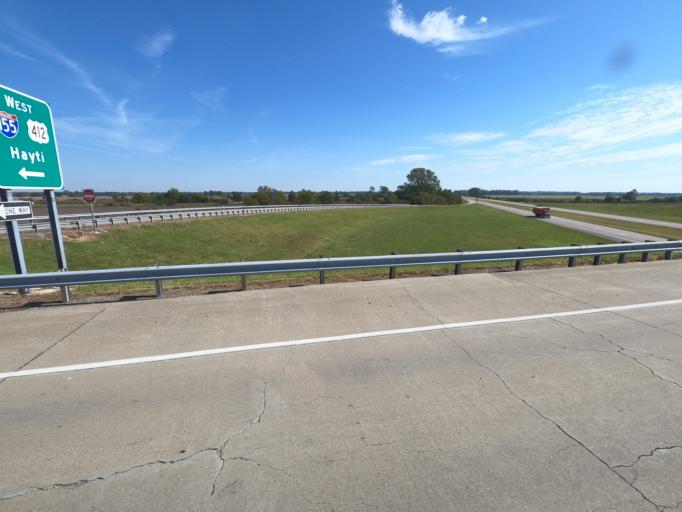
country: US
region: Missouri
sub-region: Pemiscot County
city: Caruthersville
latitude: 36.1522
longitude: -89.6637
